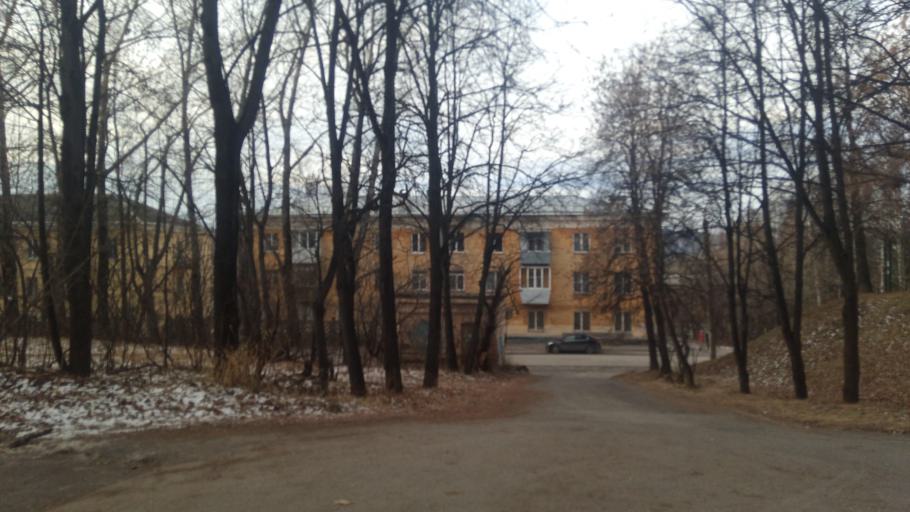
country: RU
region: Chelyabinsk
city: Zlatoust
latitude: 55.1090
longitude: 59.7192
